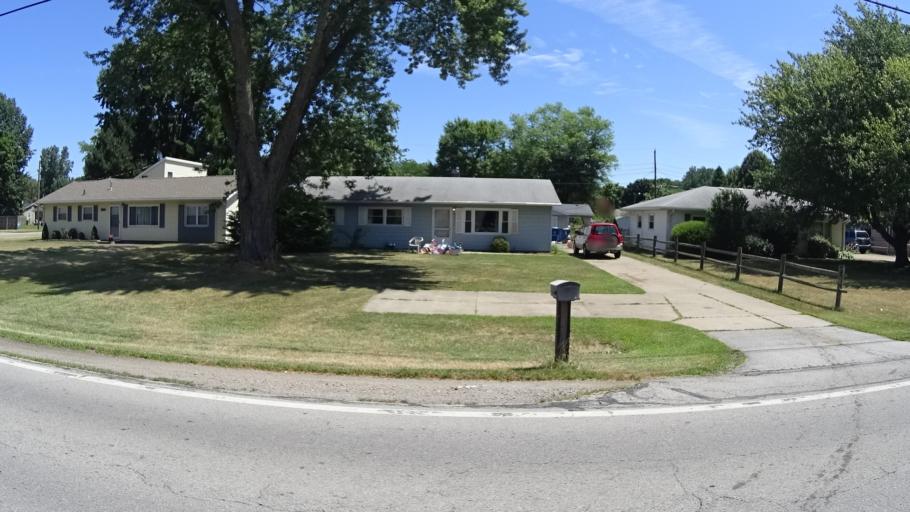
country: US
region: Ohio
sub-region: Erie County
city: Sandusky
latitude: 41.3990
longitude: -82.6766
